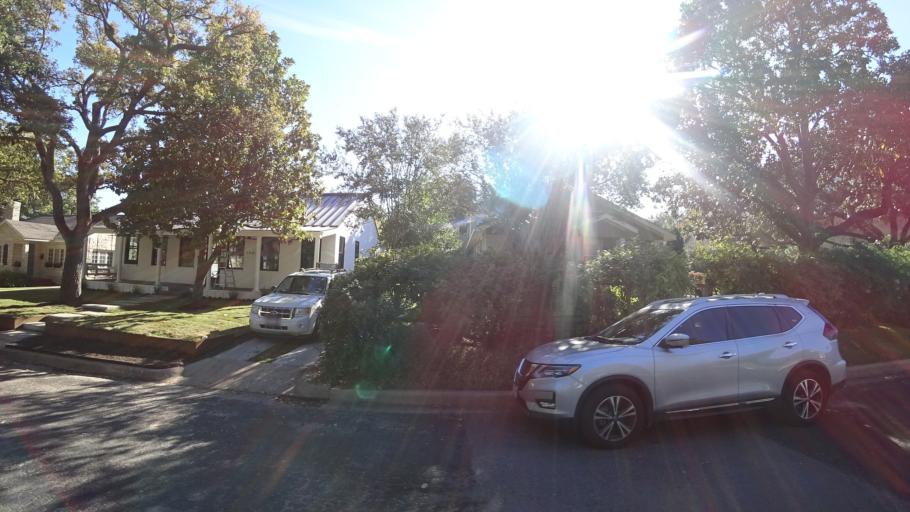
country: US
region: Texas
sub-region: Travis County
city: Austin
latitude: 30.3010
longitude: -97.7514
